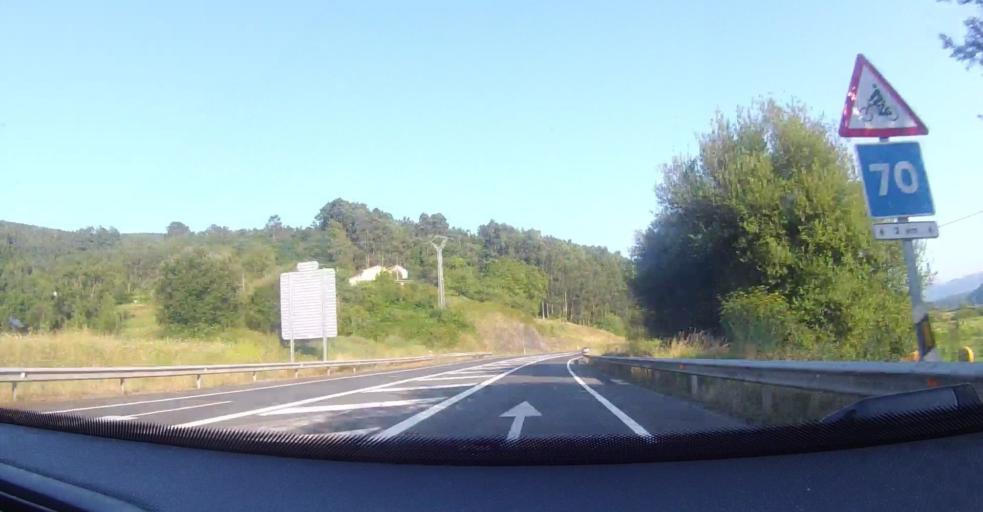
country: ES
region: Cantabria
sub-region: Provincia de Cantabria
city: Colindres
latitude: 43.3841
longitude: -3.4413
